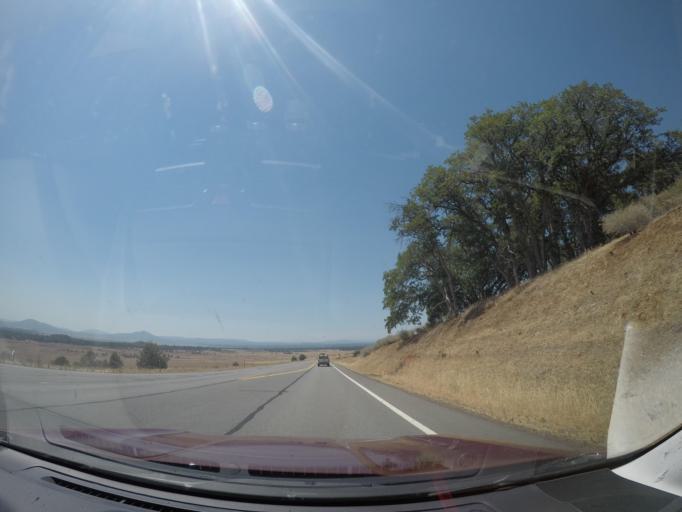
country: US
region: California
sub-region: Shasta County
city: Burney
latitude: 41.0942
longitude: -121.2778
